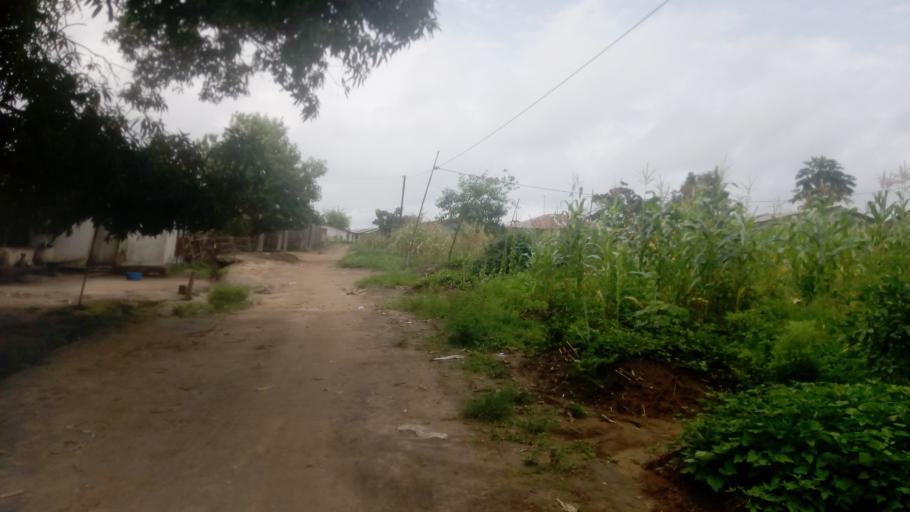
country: SL
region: Northern Province
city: Lunsar
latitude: 8.6926
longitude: -12.5401
